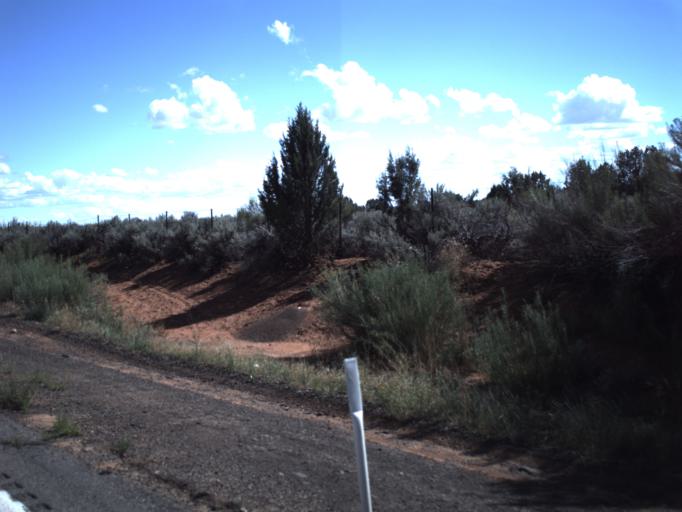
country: US
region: Arizona
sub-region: Mohave County
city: Colorado City
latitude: 37.0928
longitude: -113.1163
